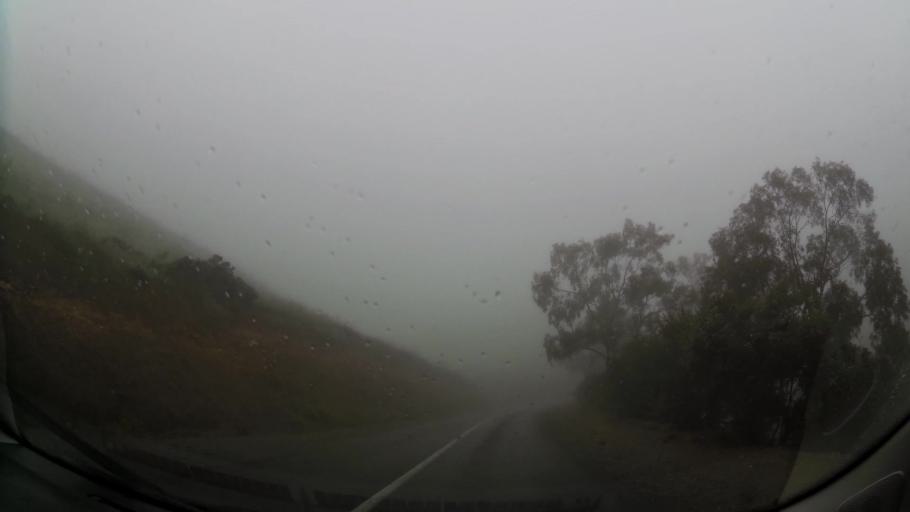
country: MA
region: Oriental
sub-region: Nador
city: Boudinar
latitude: 35.0941
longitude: -3.5365
